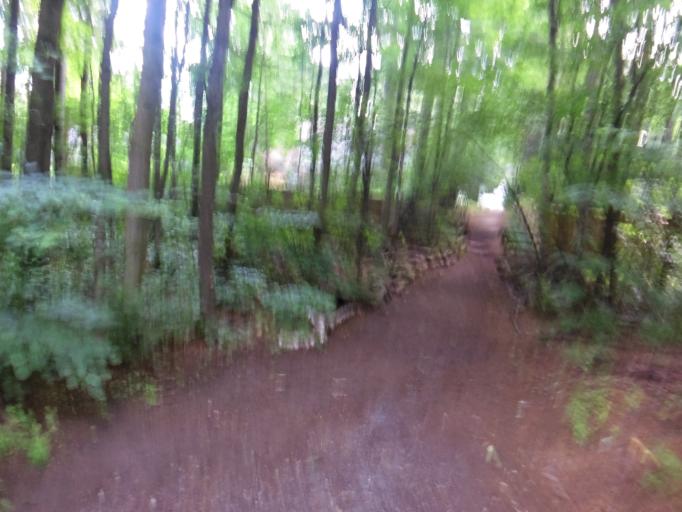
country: CA
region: Ontario
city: Bells Corners
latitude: 45.3224
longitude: -75.7929
